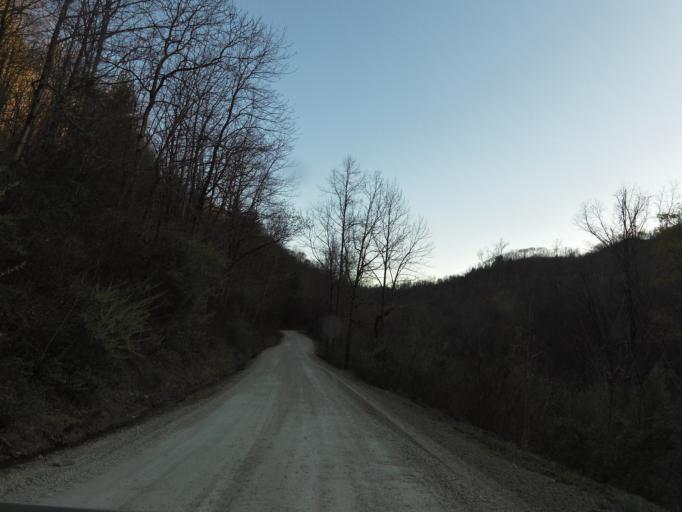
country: US
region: Tennessee
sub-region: Campbell County
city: Caryville
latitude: 36.2185
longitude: -84.3256
